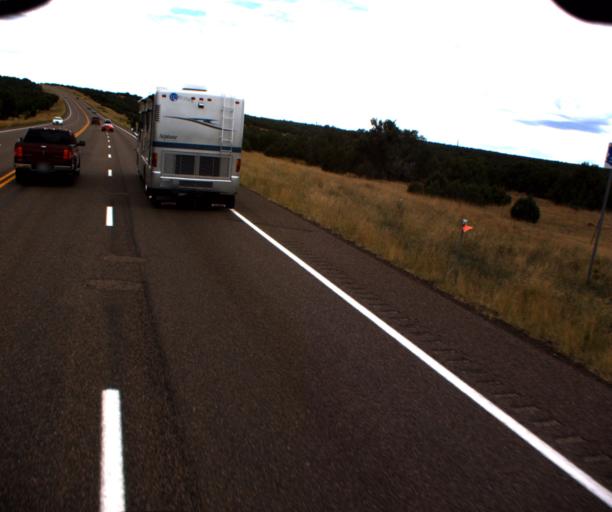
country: US
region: Arizona
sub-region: Navajo County
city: White Mountain Lake
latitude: 34.3509
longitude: -110.0533
